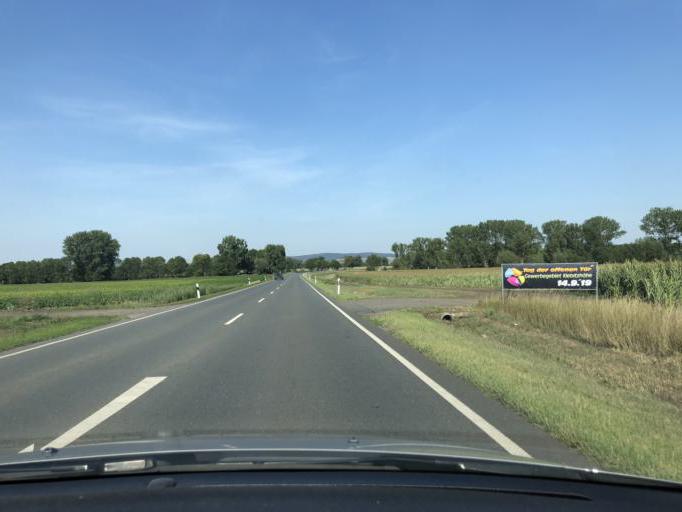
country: DE
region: Thuringia
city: Sprotau
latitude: 51.1677
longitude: 11.1899
